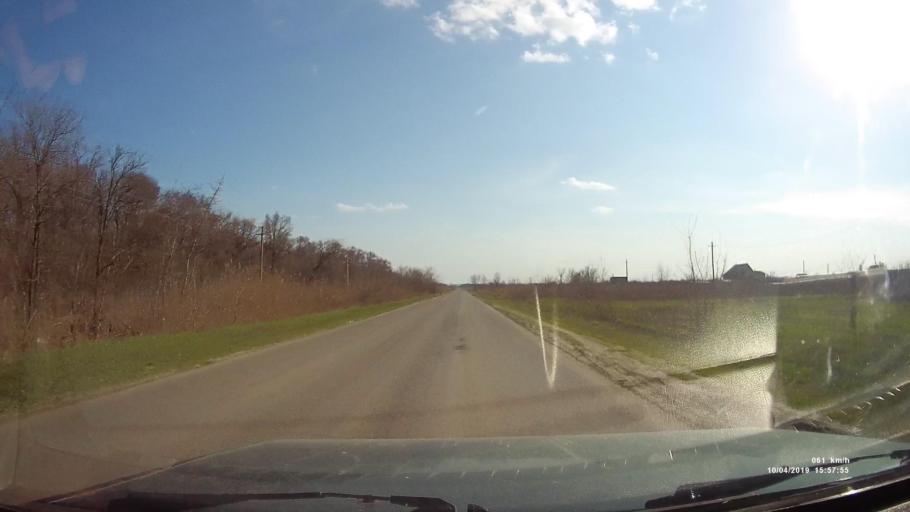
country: RU
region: Rostov
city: Masalovka
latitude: 48.4074
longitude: 40.2743
